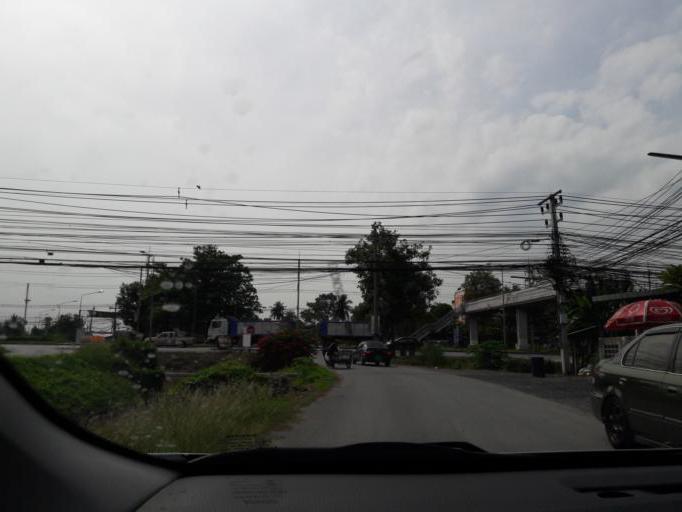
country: TH
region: Ang Thong
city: Ang Thong
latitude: 14.5795
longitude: 100.4742
